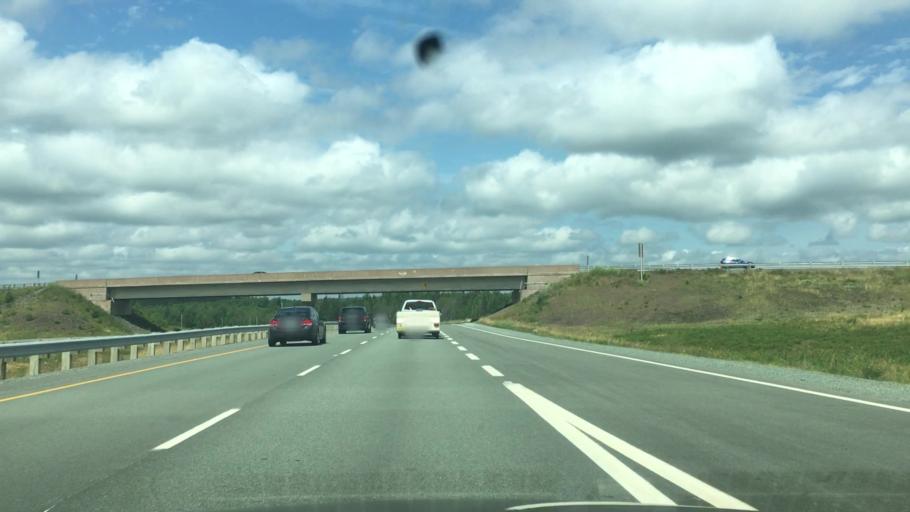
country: CA
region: Nova Scotia
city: Oxford
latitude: 45.6941
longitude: -63.7747
